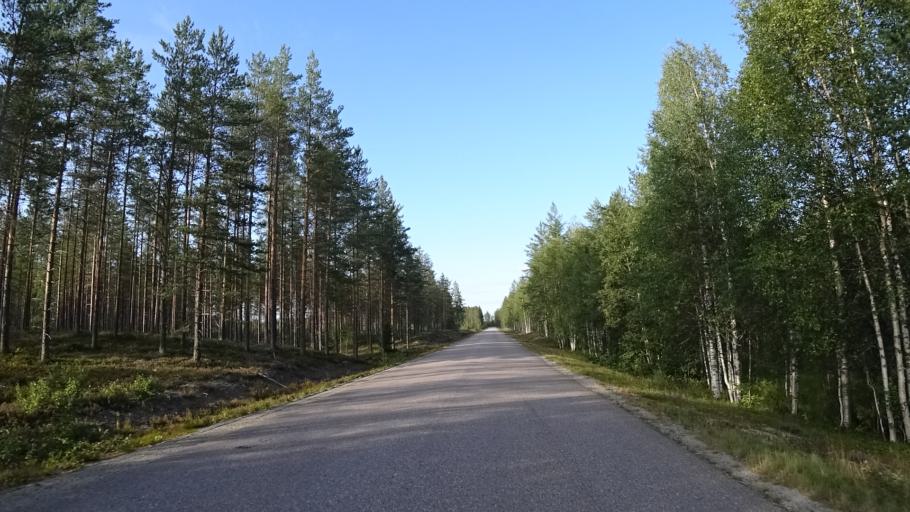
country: FI
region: North Karelia
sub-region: Joensuu
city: Eno
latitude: 63.0792
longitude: 30.5822
